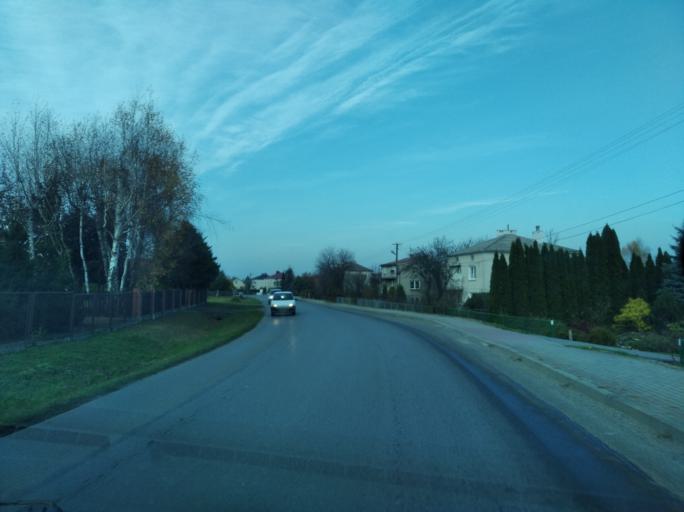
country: PL
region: Subcarpathian Voivodeship
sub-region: Powiat ropczycko-sedziszowski
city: Iwierzyce
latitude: 50.0511
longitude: 21.7461
